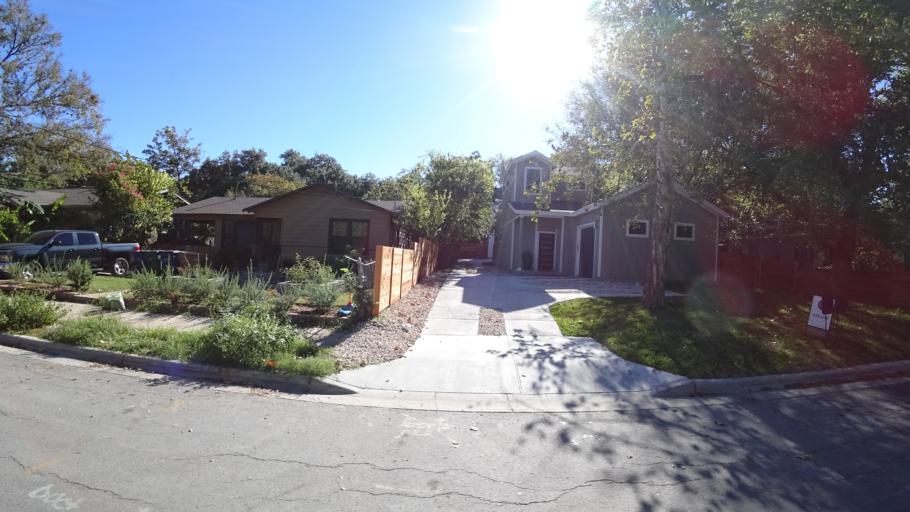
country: US
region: Texas
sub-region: Travis County
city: Austin
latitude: 30.2370
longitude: -97.7582
